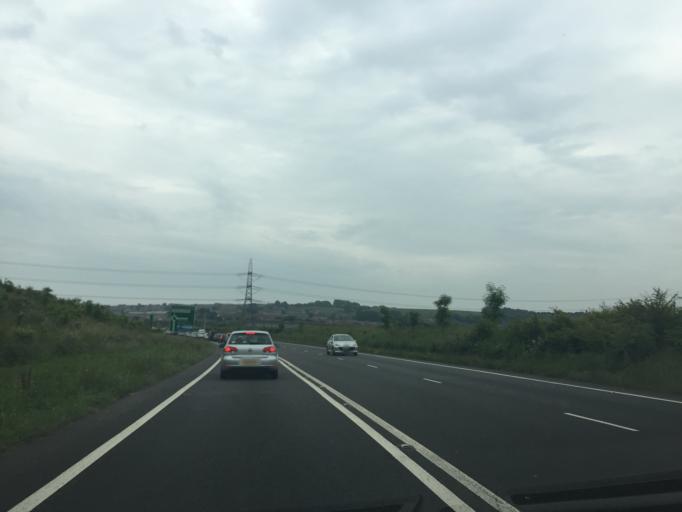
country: GB
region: England
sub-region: Dorset
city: Overcombe
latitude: 50.6550
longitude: -2.4620
